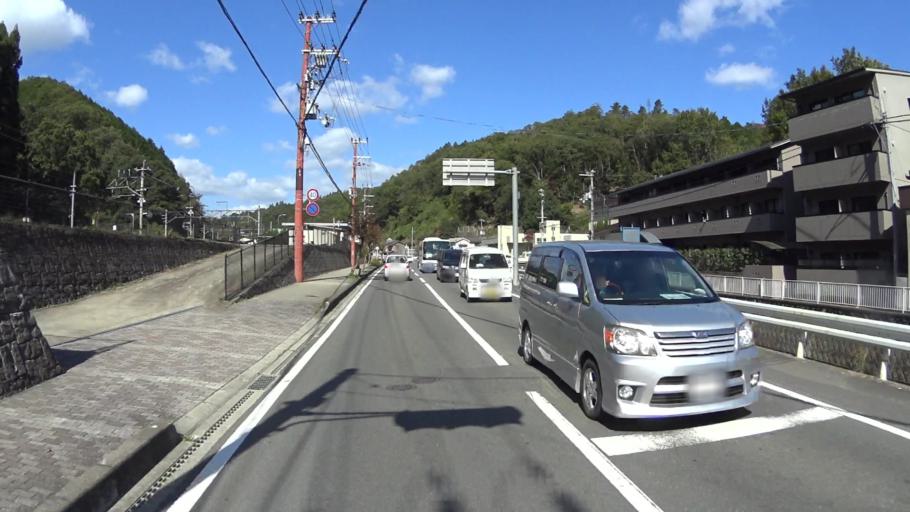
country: JP
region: Kyoto
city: Kameoka
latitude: 35.1609
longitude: 135.5047
